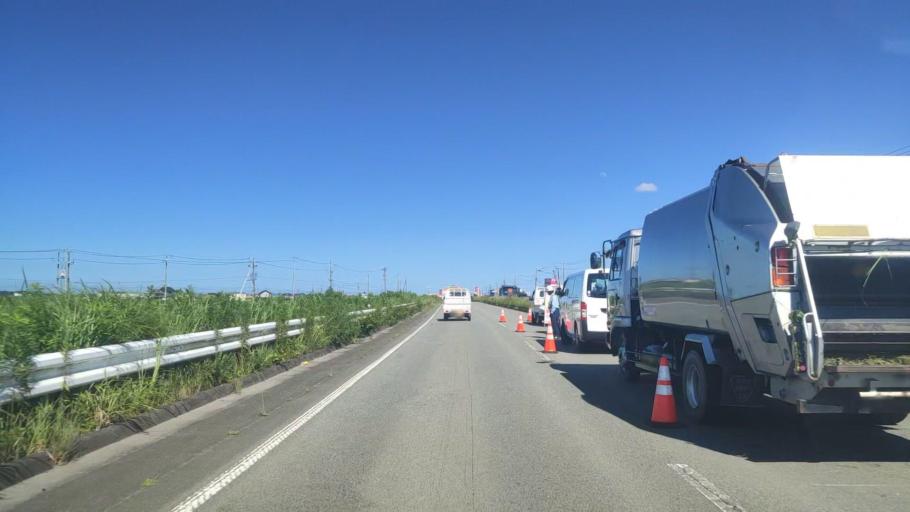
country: JP
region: Mie
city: Ise
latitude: 34.5855
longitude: 136.6058
